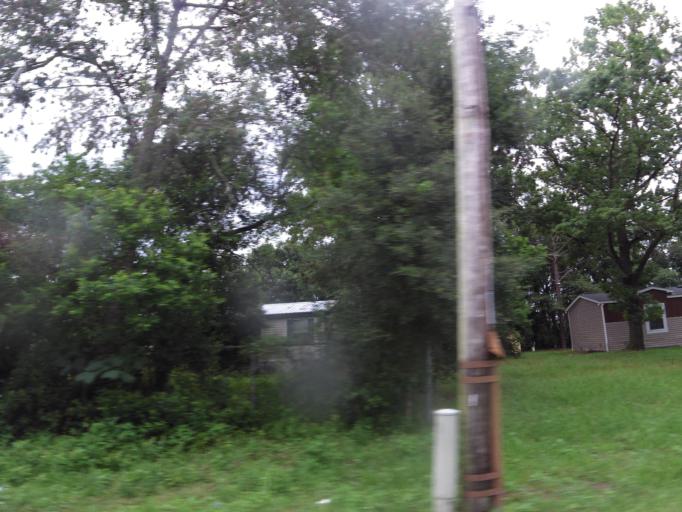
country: US
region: Florida
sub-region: Duval County
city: Jacksonville
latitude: 30.2669
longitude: -81.5389
